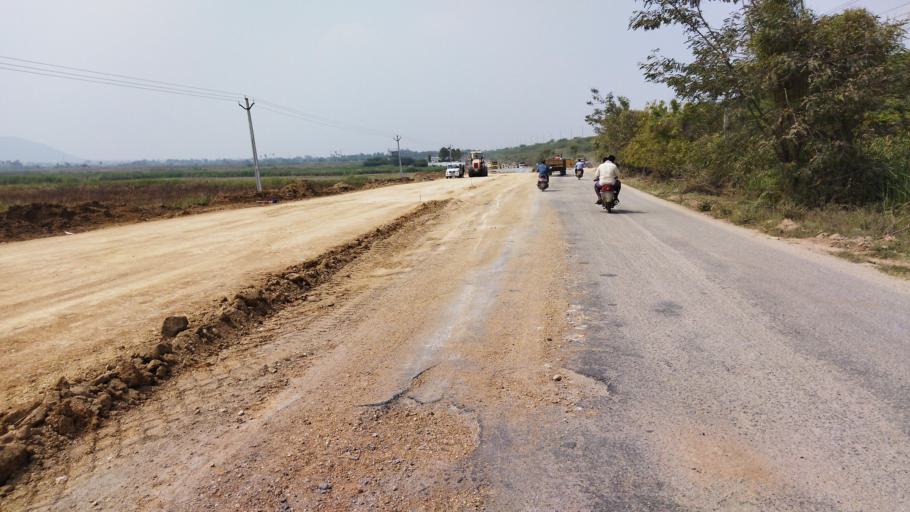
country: IN
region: Telangana
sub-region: Nalgonda
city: Nalgonda
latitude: 17.0785
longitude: 79.3086
